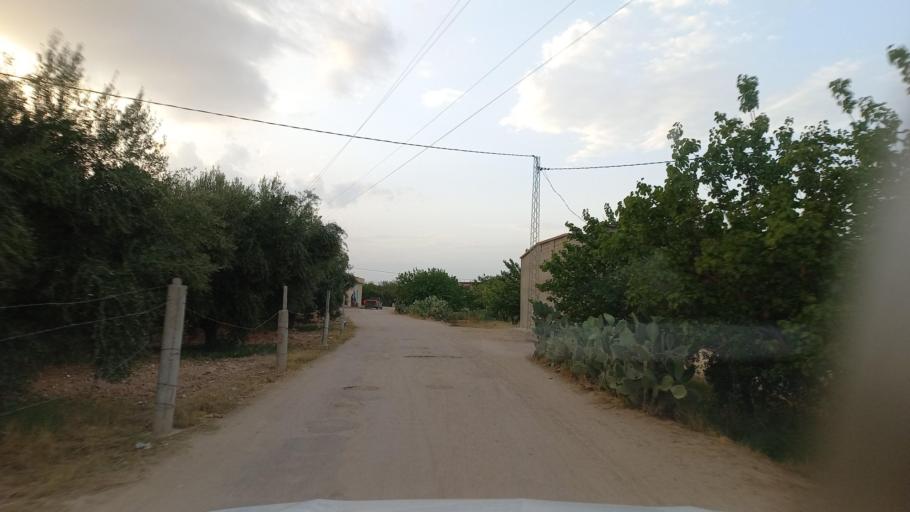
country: TN
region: Al Qasrayn
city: Kasserine
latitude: 35.2721
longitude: 9.0545
